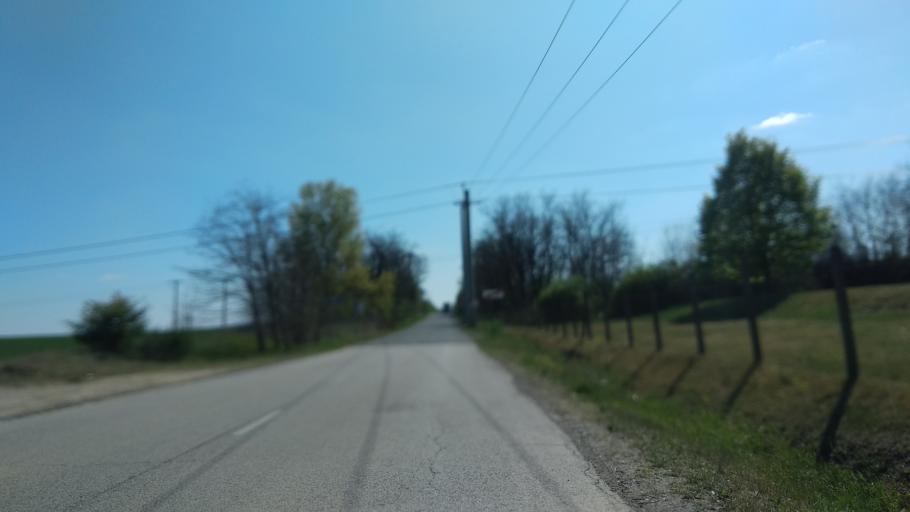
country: HU
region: Pest
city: Godollo
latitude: 47.5860
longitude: 19.3429
